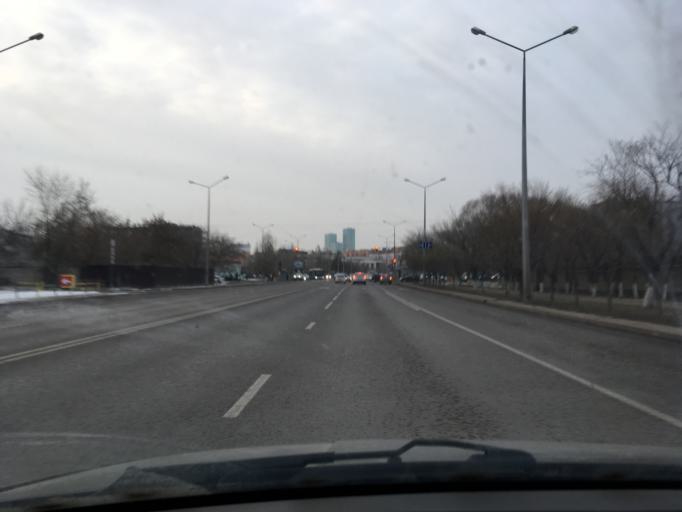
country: KZ
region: Astana Qalasy
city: Astana
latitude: 51.1578
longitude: 71.4459
